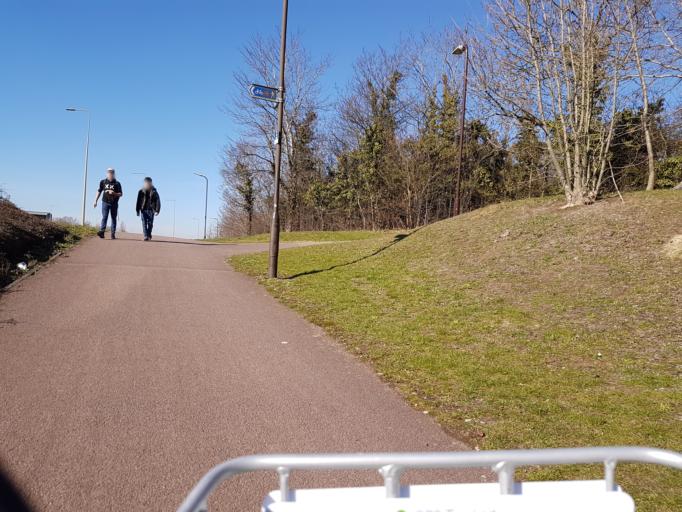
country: GB
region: England
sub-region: Milton Keynes
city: Milton Keynes
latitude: 52.0209
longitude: -0.7516
